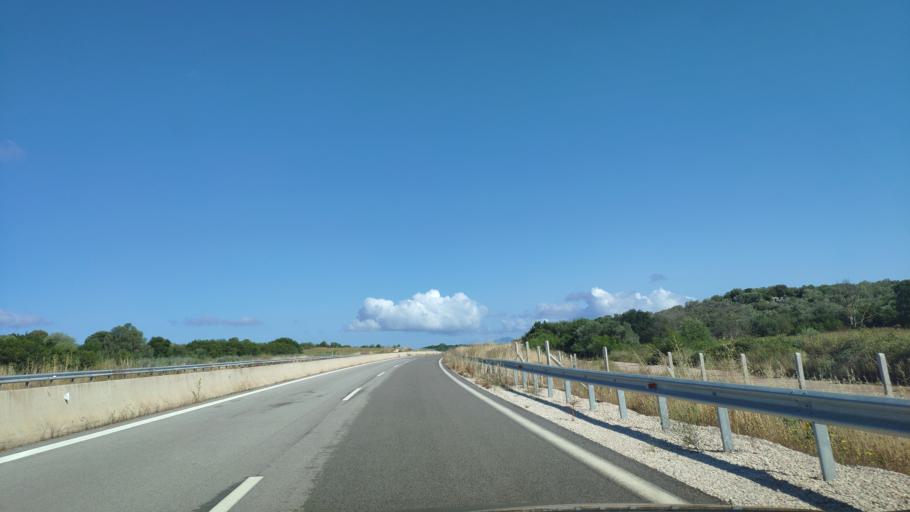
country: GR
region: West Greece
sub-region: Nomos Aitolias kai Akarnanias
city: Vonitsa
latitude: 38.9062
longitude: 20.8510
